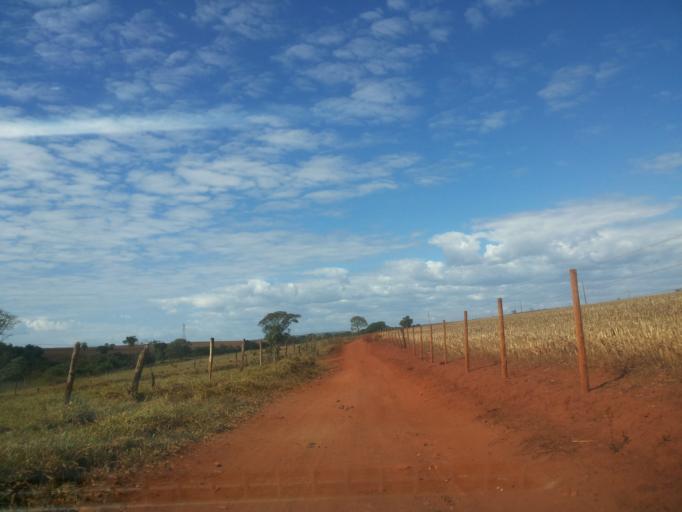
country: BR
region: Minas Gerais
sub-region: Centralina
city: Centralina
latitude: -18.5515
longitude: -49.2394
